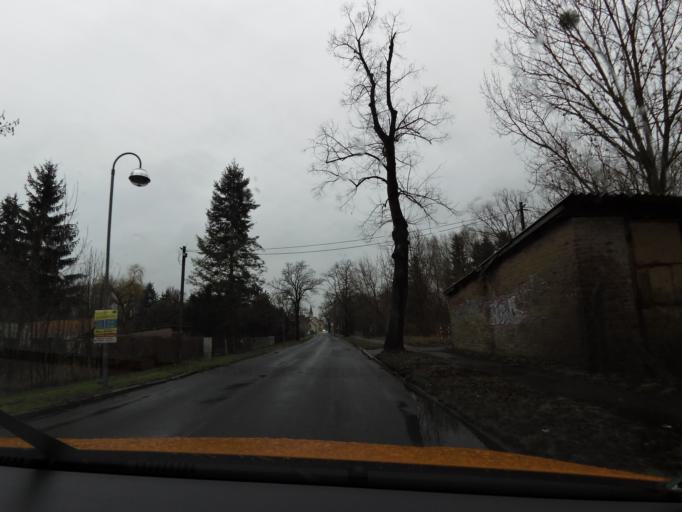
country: DE
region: Brandenburg
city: Zossen
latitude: 52.2121
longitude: 13.4436
